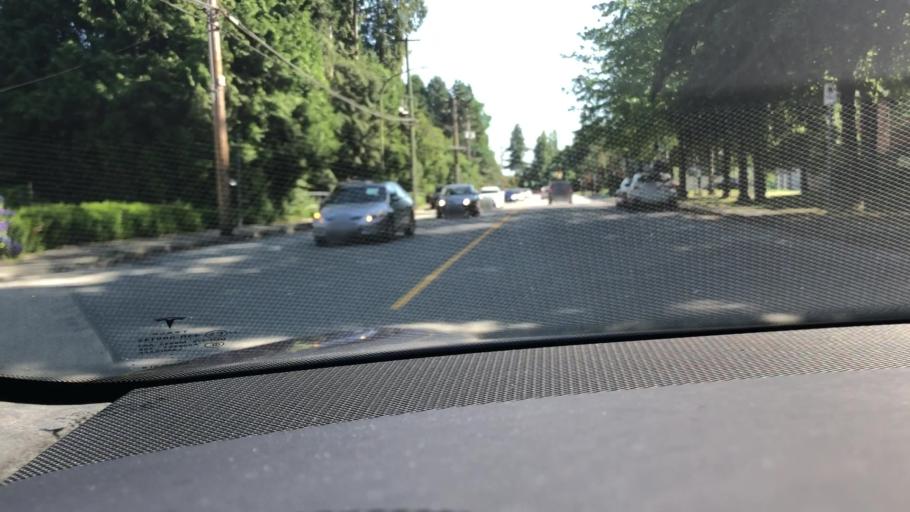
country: CA
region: British Columbia
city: Burnaby
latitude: 49.2484
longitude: -122.9747
